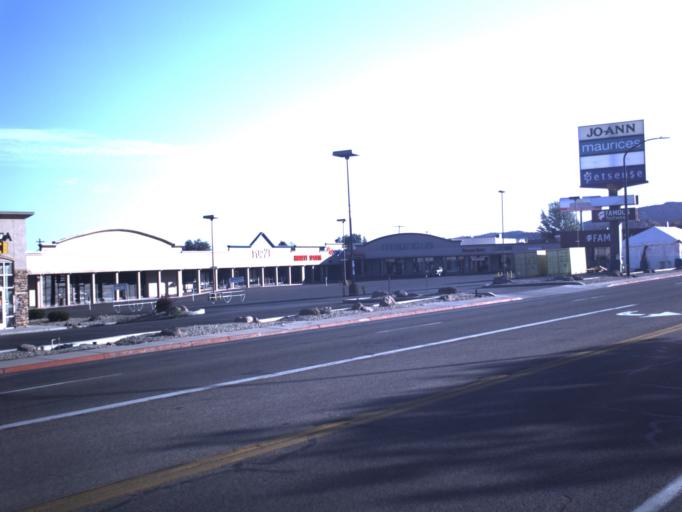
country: US
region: Utah
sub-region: Iron County
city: Cedar City
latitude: 37.6658
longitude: -113.0642
